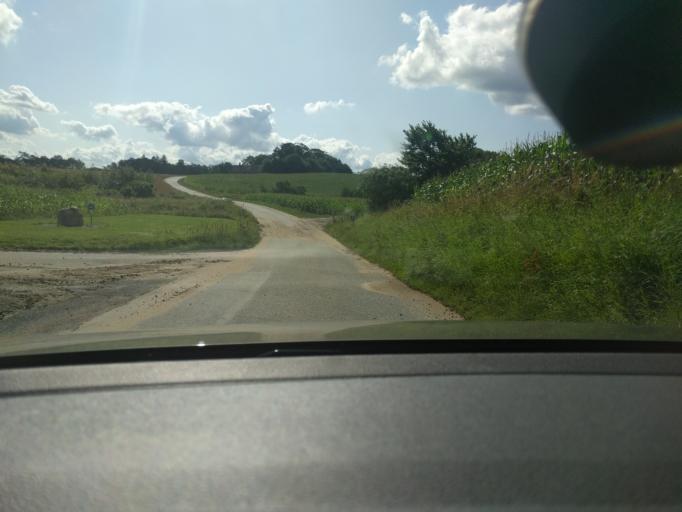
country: DK
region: Central Jutland
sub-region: Viborg Kommune
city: Viborg
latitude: 56.5265
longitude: 9.3486
